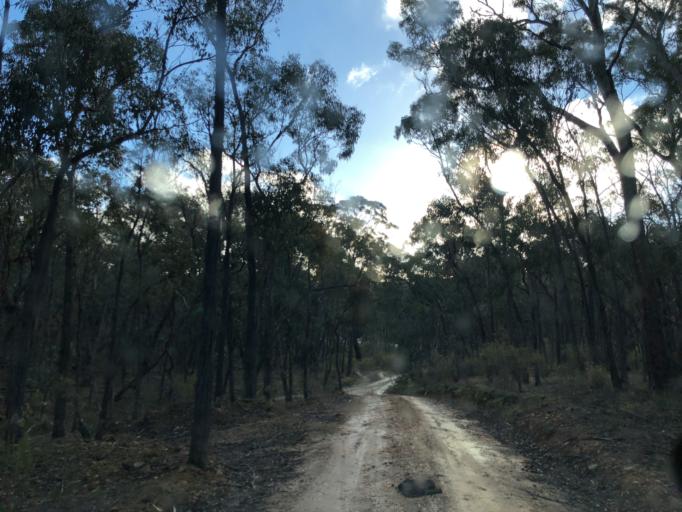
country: AU
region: Victoria
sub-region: Mount Alexander
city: Castlemaine
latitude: -37.2204
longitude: 144.2639
